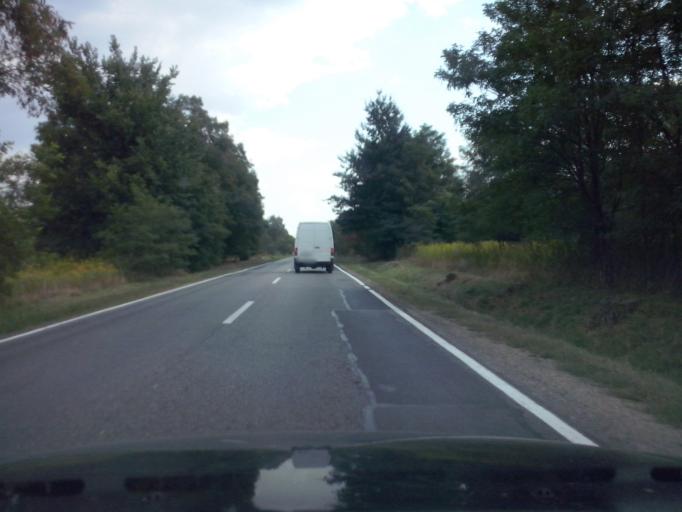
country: PL
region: Subcarpathian Voivodeship
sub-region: Powiat nizanski
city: Bieliny
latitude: 50.4136
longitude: 22.2826
